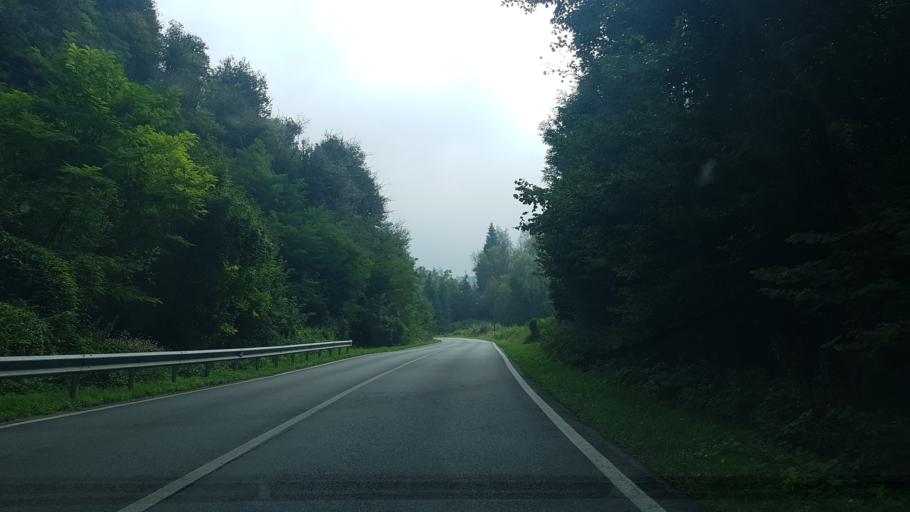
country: IT
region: Piedmont
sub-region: Provincia di Cuneo
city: Chiusa di Pesio
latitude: 44.3164
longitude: 7.6905
